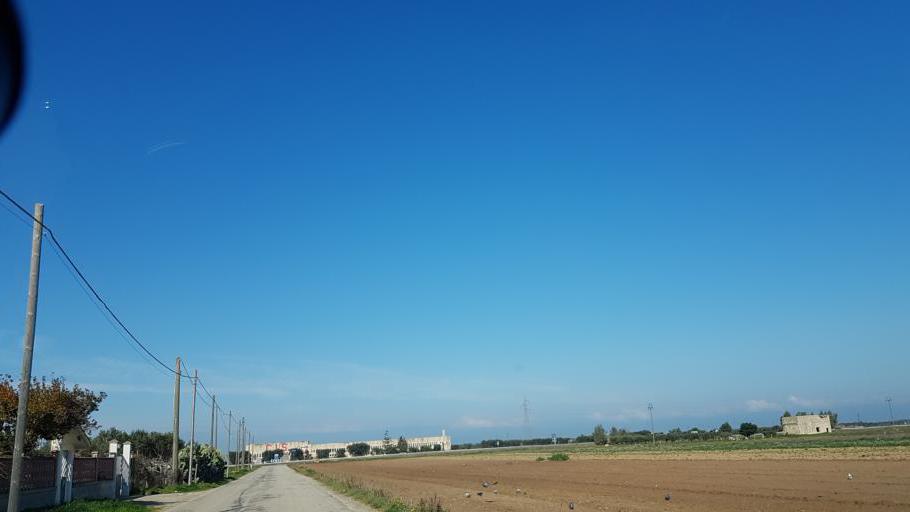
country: IT
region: Apulia
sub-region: Provincia di Brindisi
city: Brindisi
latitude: 40.6059
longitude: 17.8905
